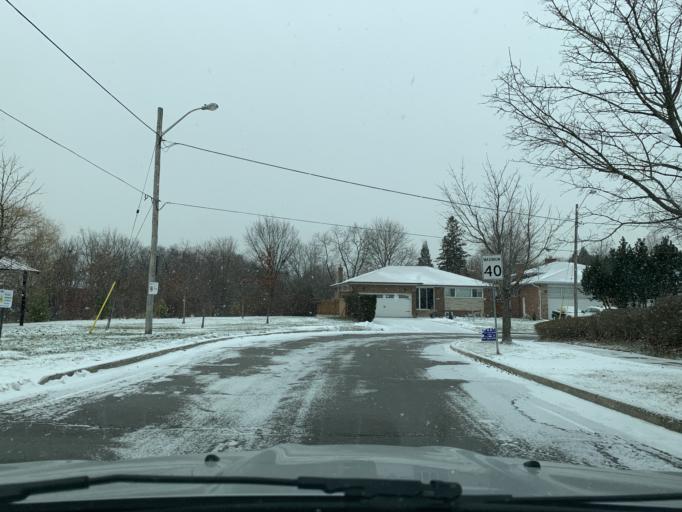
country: CA
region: Ontario
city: Concord
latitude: 43.7398
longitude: -79.4881
